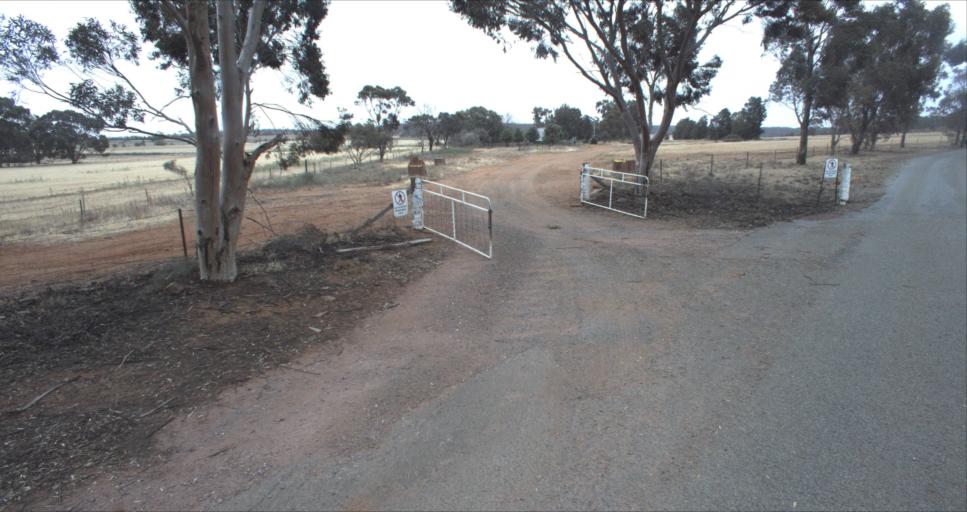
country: AU
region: New South Wales
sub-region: Leeton
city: Leeton
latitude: -34.4517
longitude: 146.3941
